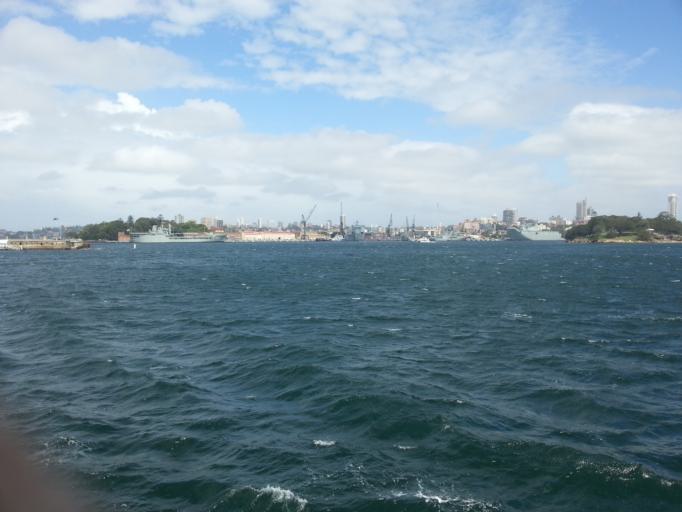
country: AU
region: New South Wales
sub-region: North Sydney
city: Kirribilli
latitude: -33.8532
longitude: 151.2226
